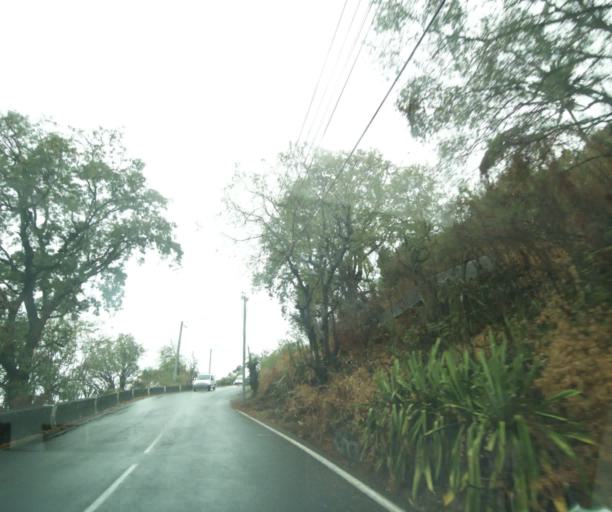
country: RE
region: Reunion
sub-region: Reunion
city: Saint-Paul
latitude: -21.0158
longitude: 55.2839
